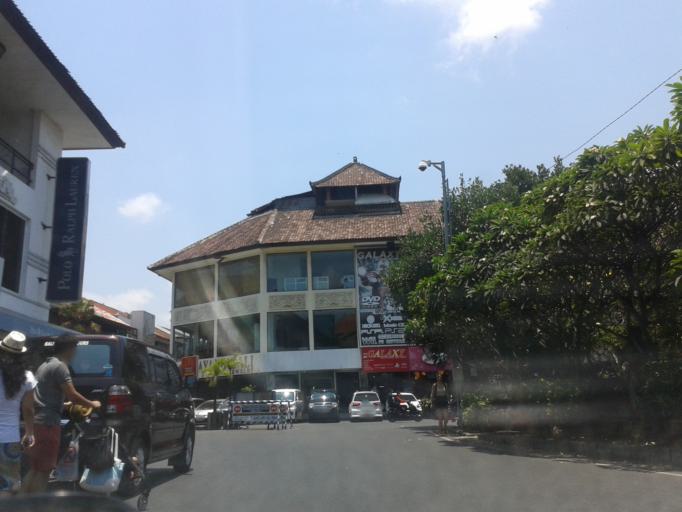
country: ID
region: Bali
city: Kuta
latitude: -8.7247
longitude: 115.1714
